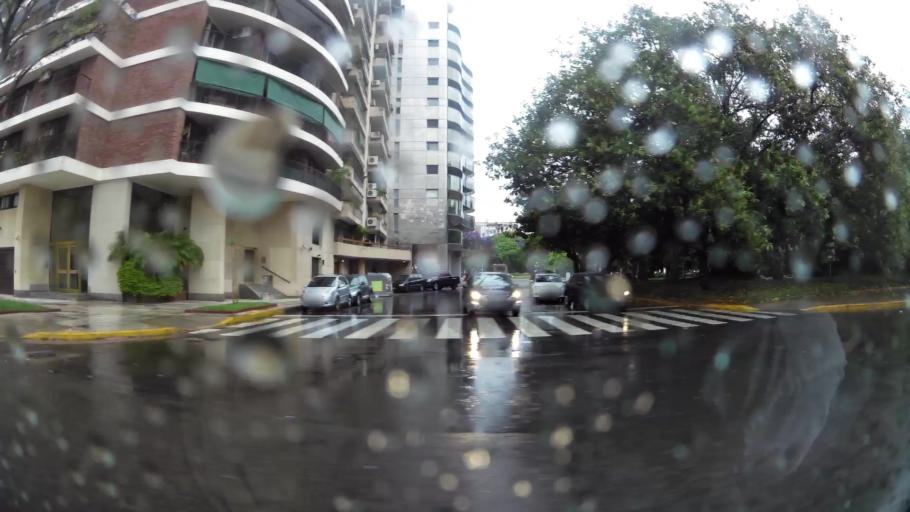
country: AR
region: Buenos Aires F.D.
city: Retiro
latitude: -34.5798
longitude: -58.4002
